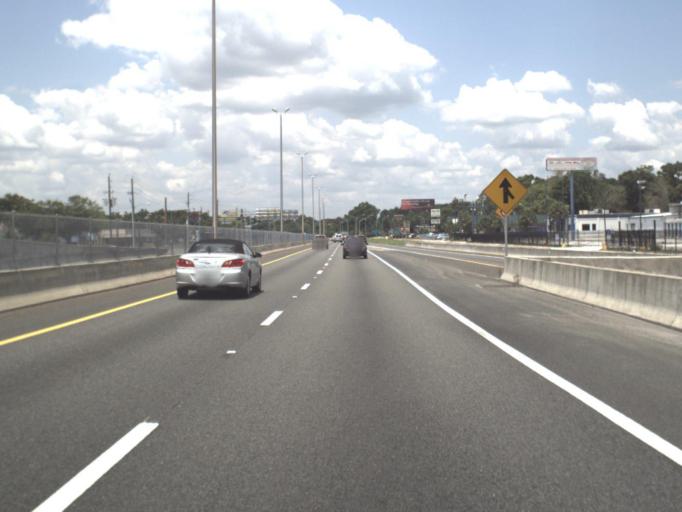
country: US
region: Florida
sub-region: Duval County
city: Jacksonville
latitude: 30.3249
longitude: -81.5631
